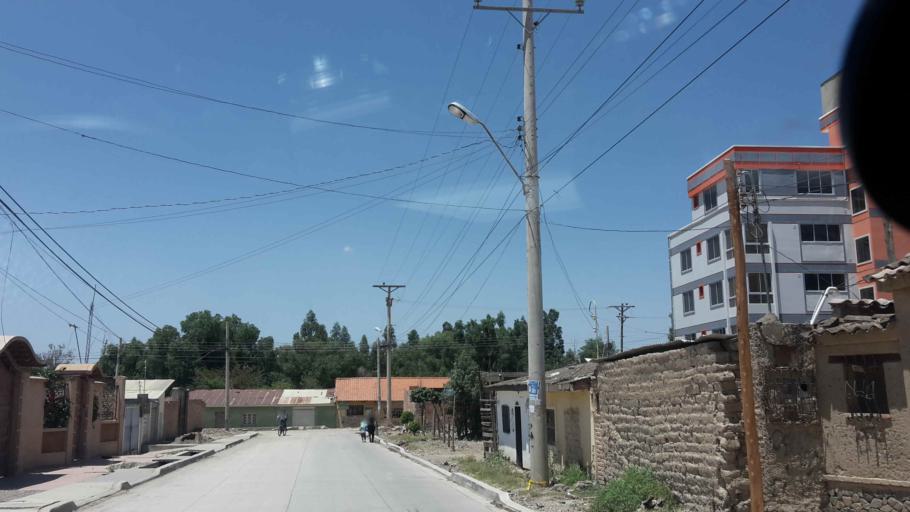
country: BO
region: Cochabamba
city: Cochabamba
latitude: -17.3554
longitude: -66.2076
